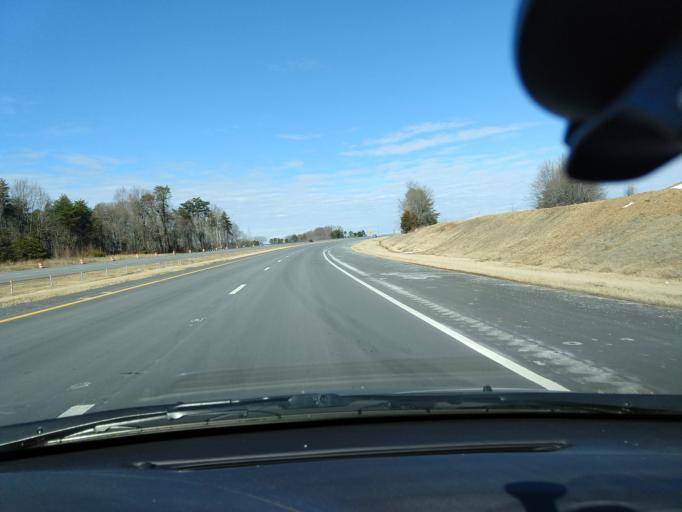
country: US
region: North Carolina
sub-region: Guilford County
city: Oak Ridge
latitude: 36.1289
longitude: -79.9655
